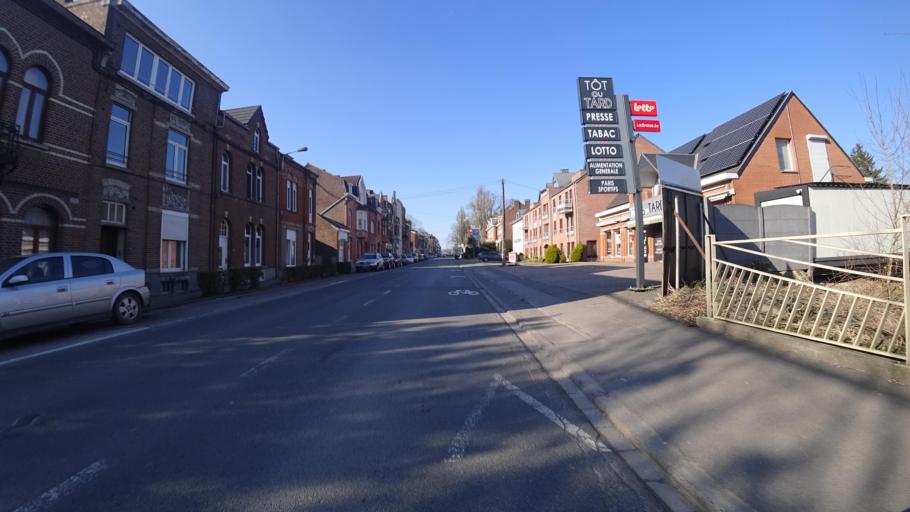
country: BE
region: Wallonia
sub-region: Province de Namur
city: Gembloux
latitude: 50.5648
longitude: 4.6966
